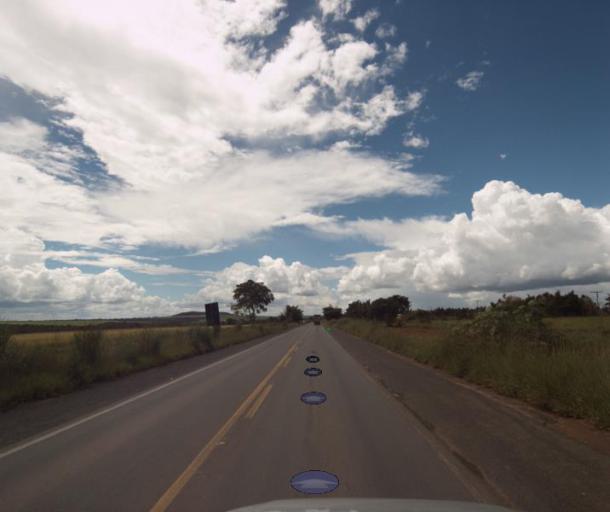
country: BR
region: Goias
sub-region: Uruacu
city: Uruacu
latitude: -14.1600
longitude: -49.1226
